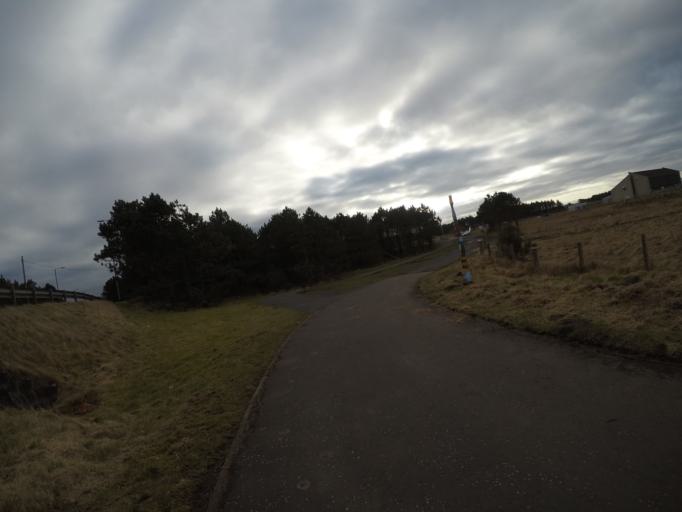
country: GB
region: Scotland
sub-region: North Ayrshire
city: Irvine
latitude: 55.5892
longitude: -4.6631
